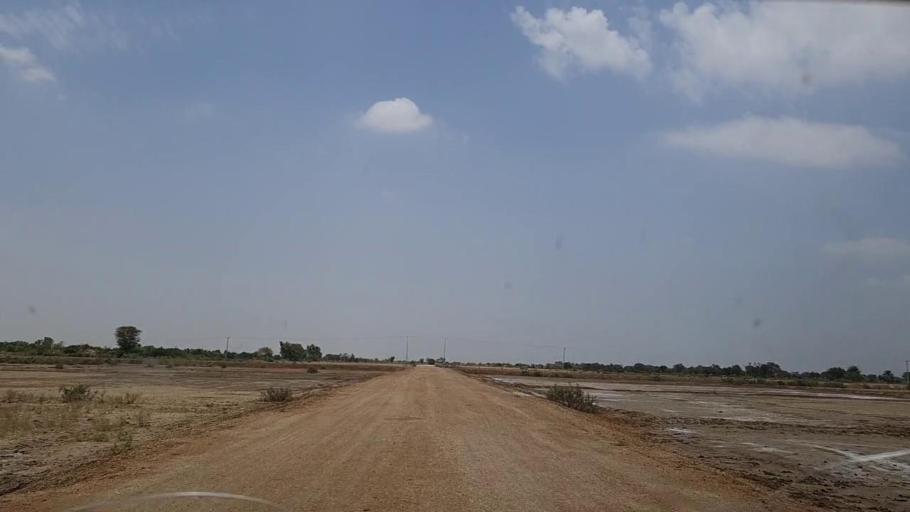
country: PK
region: Sindh
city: Phulji
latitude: 26.8157
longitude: 67.6340
